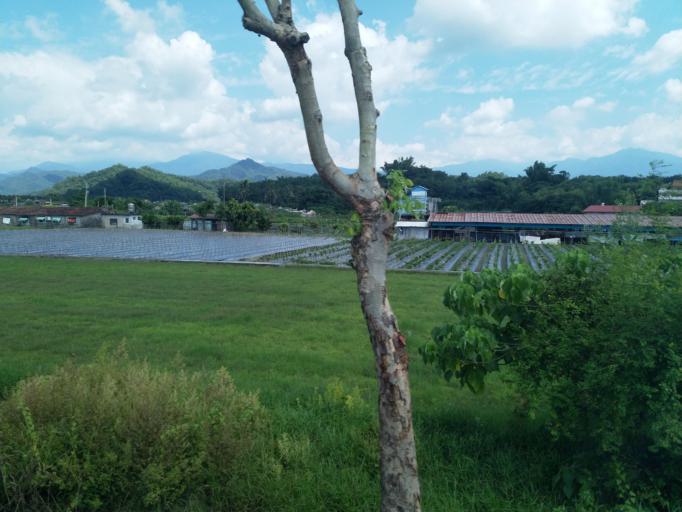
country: TW
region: Taiwan
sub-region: Pingtung
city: Pingtung
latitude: 22.8912
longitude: 120.5502
